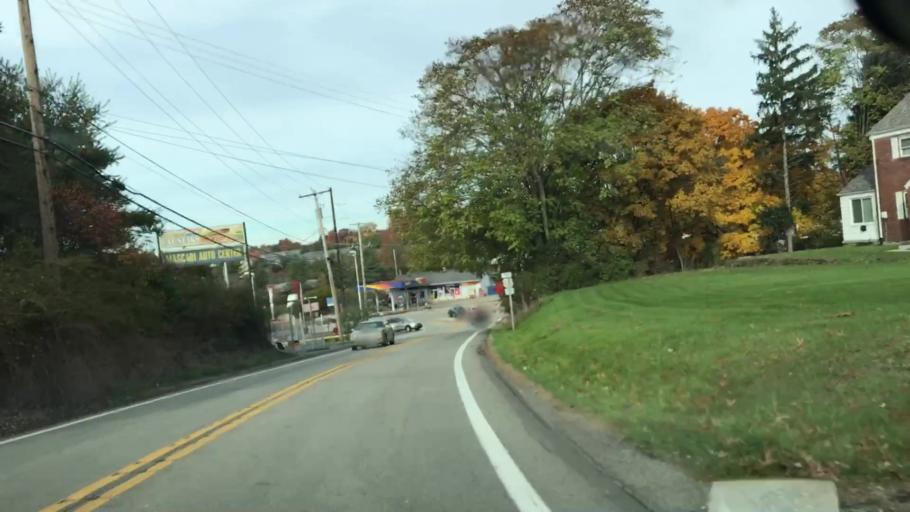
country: US
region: Pennsylvania
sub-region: Allegheny County
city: Allison Park
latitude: 40.5655
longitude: -79.9976
